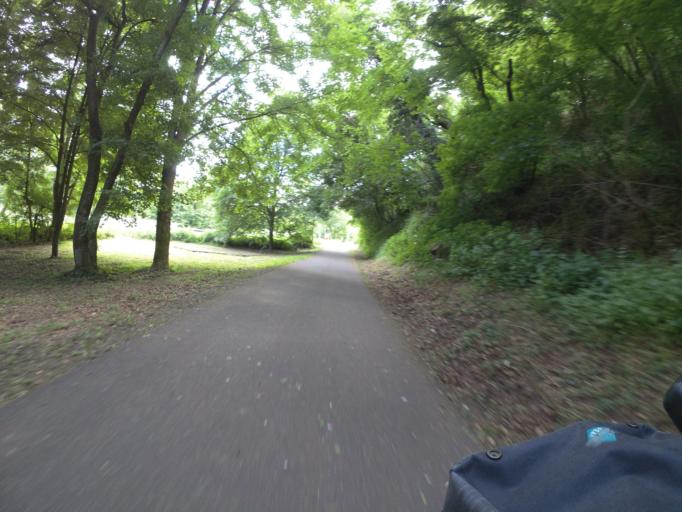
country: DE
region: Rheinland-Pfalz
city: Hochstatten
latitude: 49.7690
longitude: 7.8306
